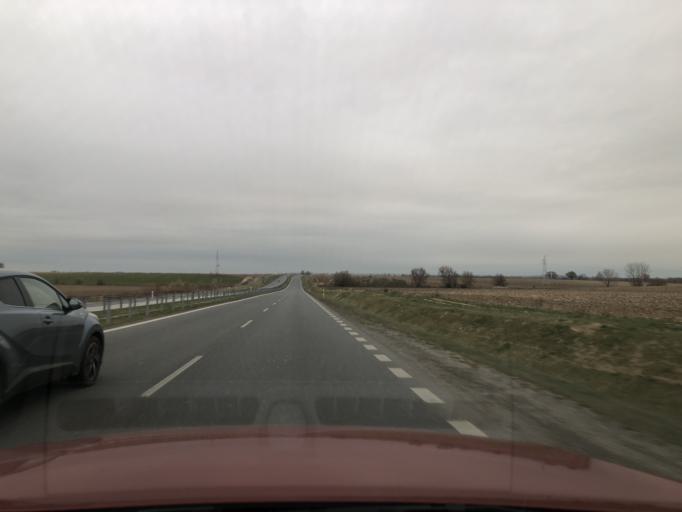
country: PL
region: Lower Silesian Voivodeship
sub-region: Powiat swidnicki
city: Swidnica
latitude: 50.8437
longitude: 16.4349
